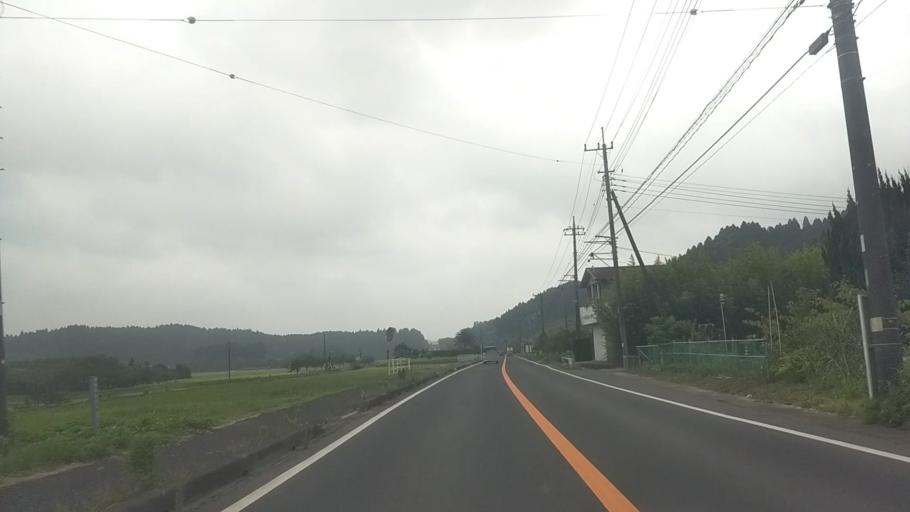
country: JP
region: Chiba
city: Ohara
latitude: 35.2760
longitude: 140.3283
